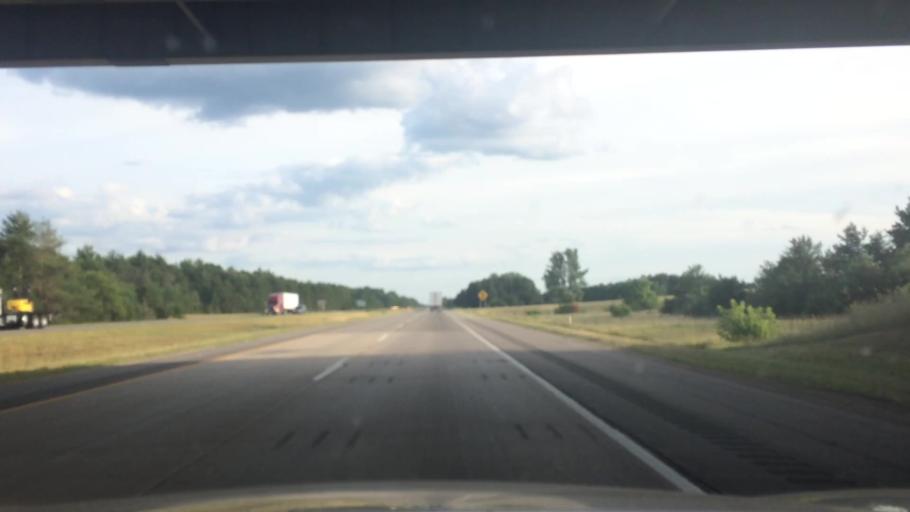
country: US
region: Wisconsin
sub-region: Portage County
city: Plover
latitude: 44.2591
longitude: -89.5241
